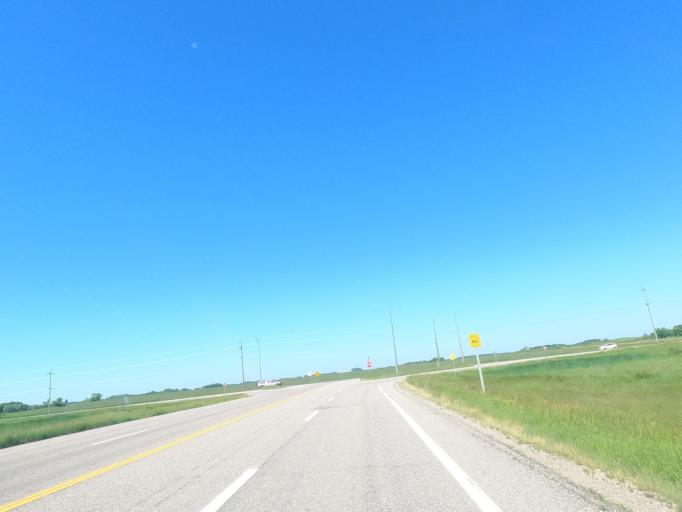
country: CA
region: Manitoba
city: Brandon
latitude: 49.5867
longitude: -99.9603
